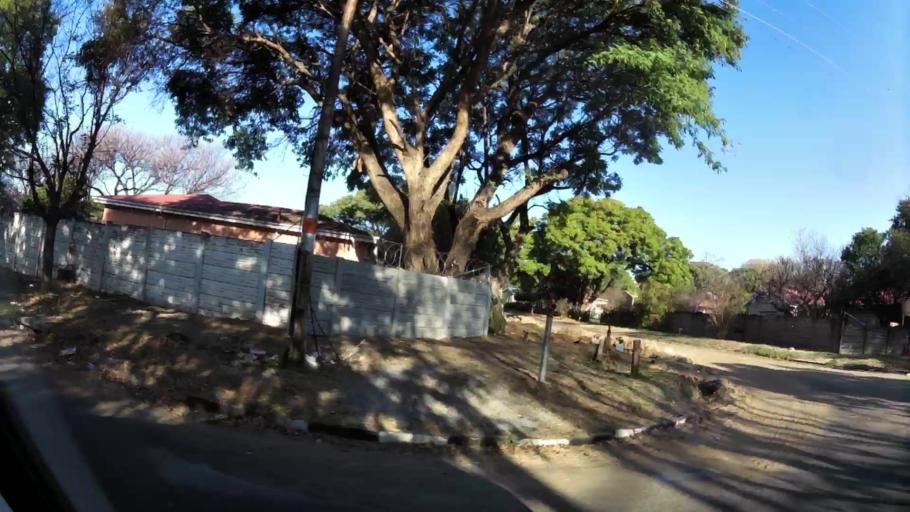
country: ZA
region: North-West
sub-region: Bojanala Platinum District Municipality
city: Rustenburg
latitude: -25.6859
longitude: 27.2309
